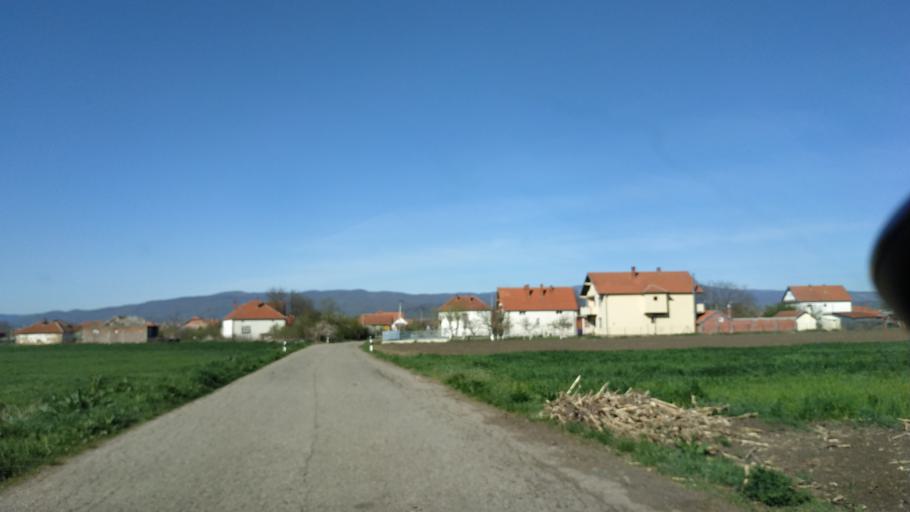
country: RS
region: Central Serbia
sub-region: Nisavski Okrug
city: Aleksinac
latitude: 43.5062
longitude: 21.6826
